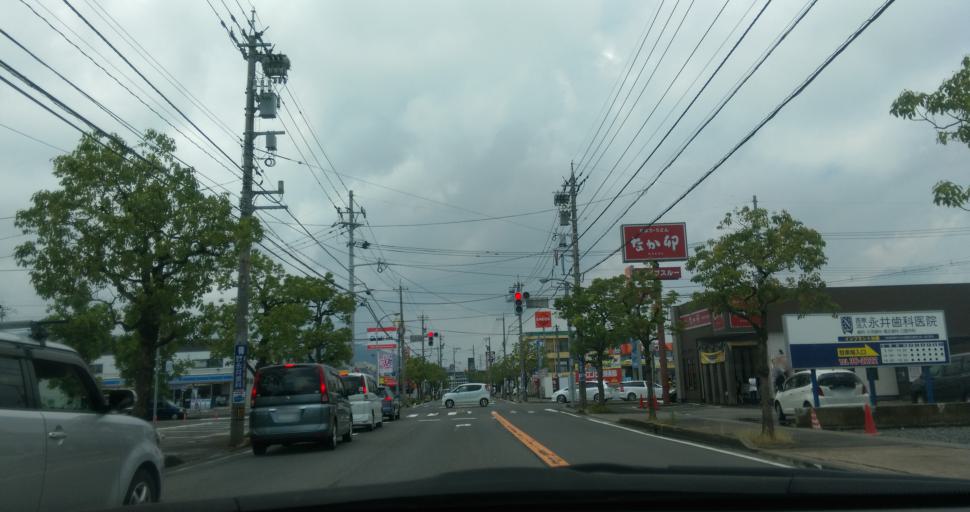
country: JP
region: Fukui
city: Fukui-shi
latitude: 36.0563
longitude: 136.1878
